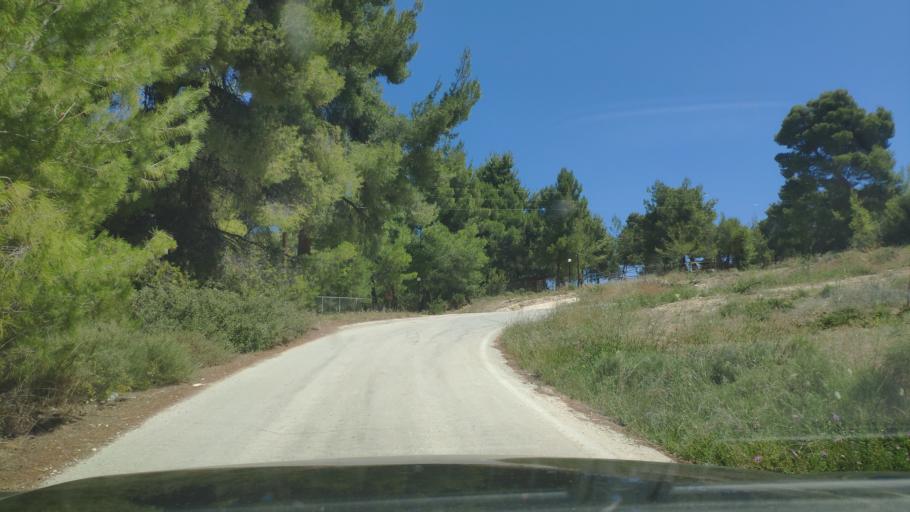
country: GR
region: Peloponnese
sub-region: Nomos Korinthias
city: Khiliomodhi
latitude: 37.8027
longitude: 22.8943
